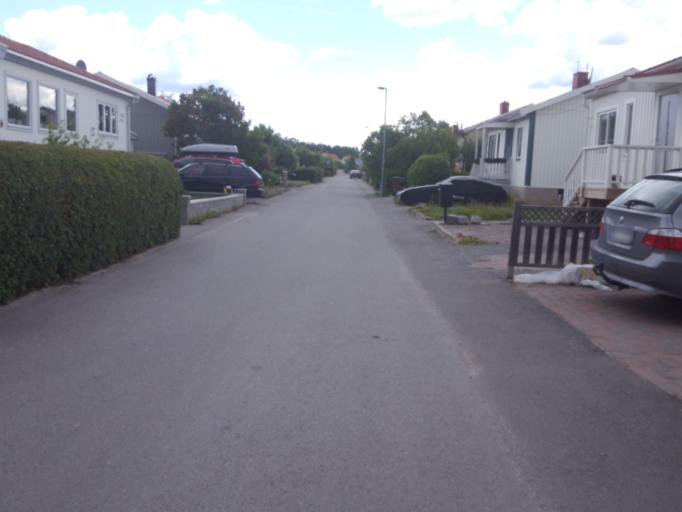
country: SE
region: Uppsala
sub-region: Uppsala Kommun
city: Uppsala
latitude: 59.8590
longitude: 17.6687
